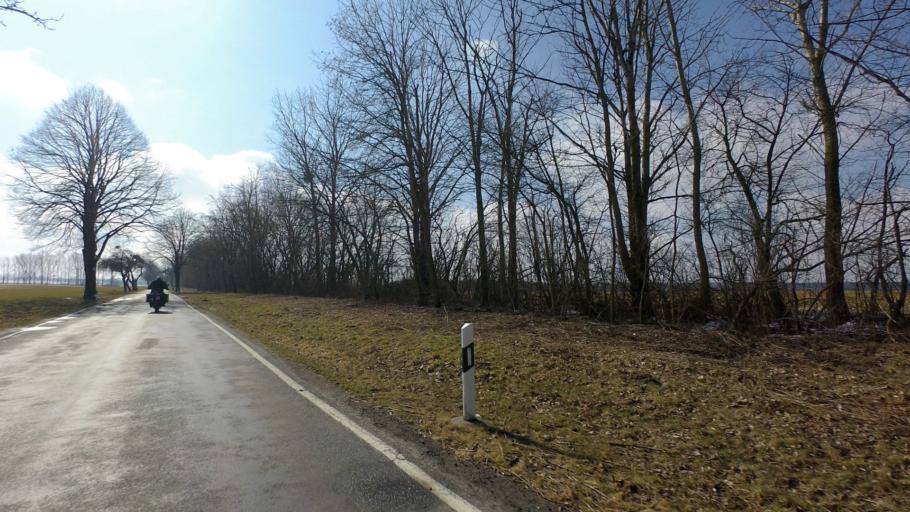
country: DE
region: Brandenburg
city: Werneuchen
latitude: 52.6986
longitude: 13.7213
